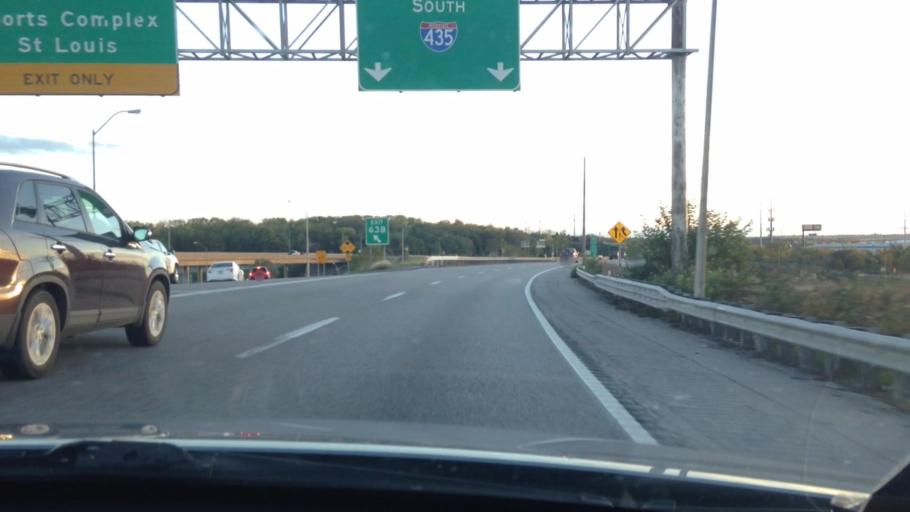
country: US
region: Missouri
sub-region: Jackson County
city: Raytown
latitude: 39.0610
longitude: -94.4889
